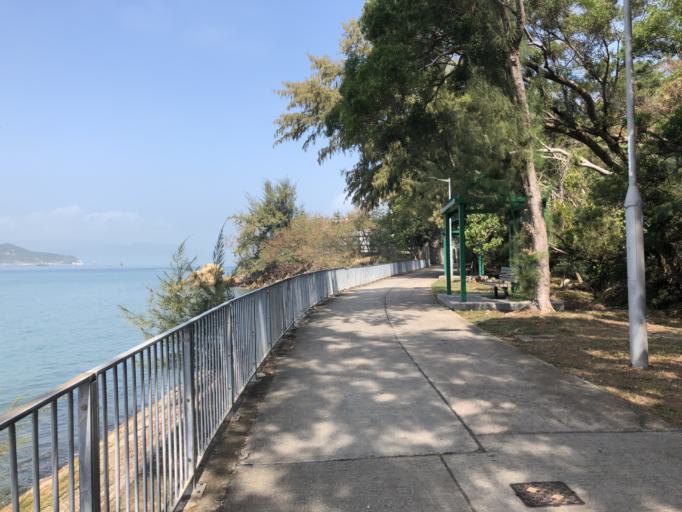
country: HK
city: Yung Shue Wan
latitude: 22.2149
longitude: 114.0254
